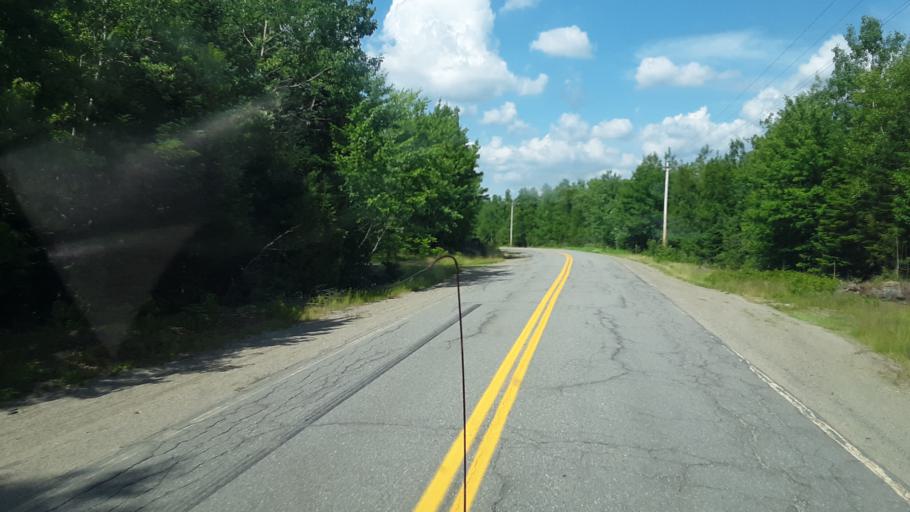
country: US
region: Maine
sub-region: Washington County
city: Calais
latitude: 45.1143
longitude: -67.5054
